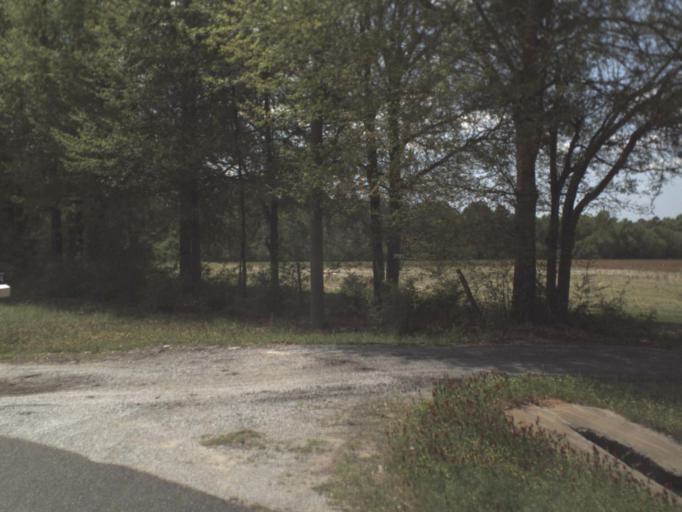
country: US
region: Florida
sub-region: Okaloosa County
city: Crestview
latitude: 30.8745
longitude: -86.6660
